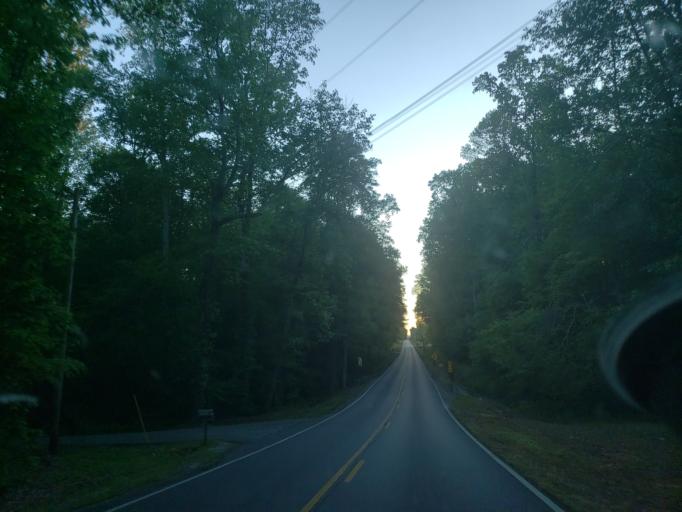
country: US
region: Alabama
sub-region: Madison County
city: Hazel Green
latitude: 34.9769
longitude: -86.6292
